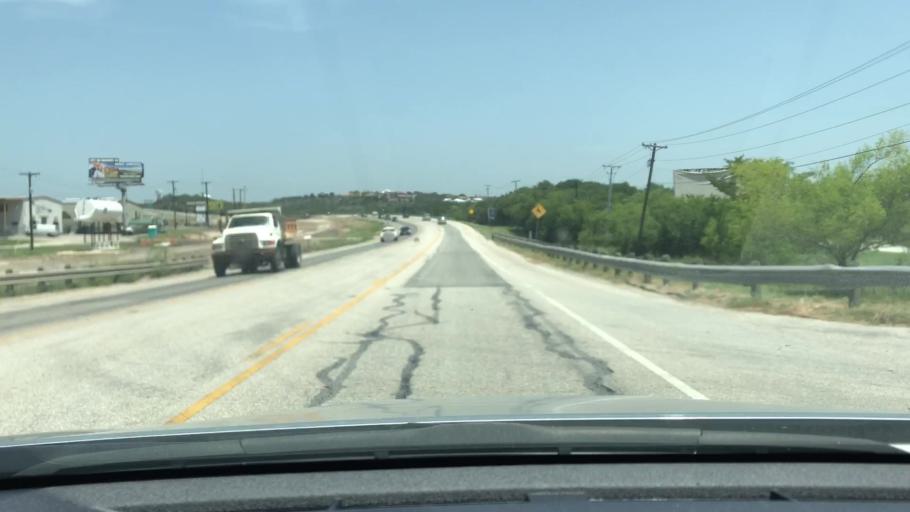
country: US
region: Texas
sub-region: Comal County
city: New Braunfels
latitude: 29.6903
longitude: -98.1550
